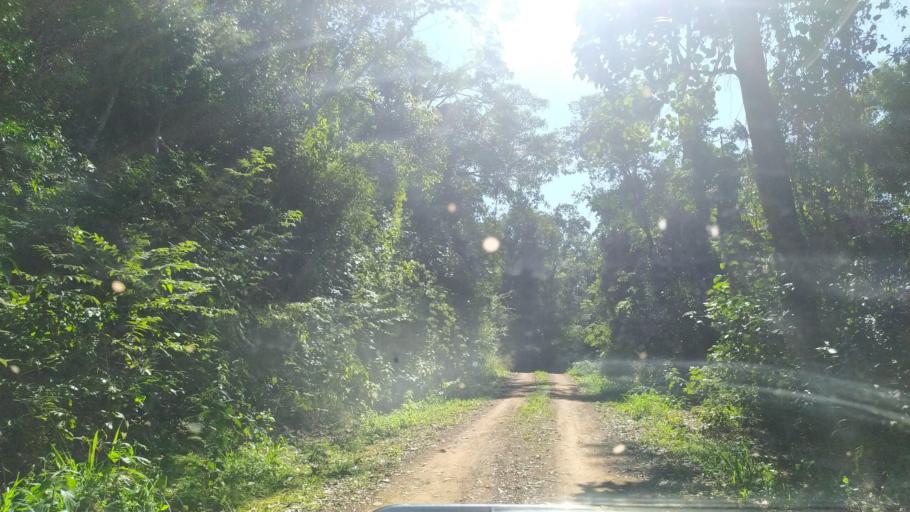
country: AR
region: Misiones
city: El Alcazar
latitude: -26.7618
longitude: -54.5779
